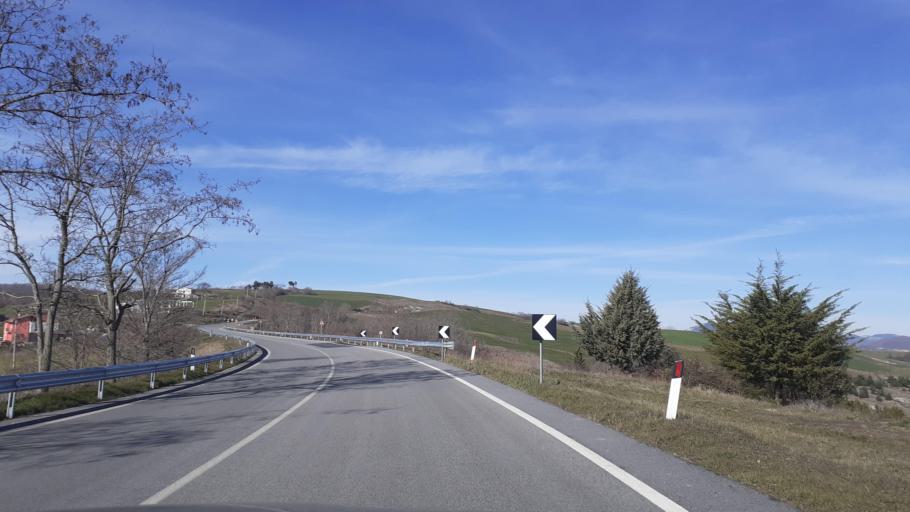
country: IT
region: Molise
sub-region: Provincia di Campobasso
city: Pietracupa
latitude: 41.6851
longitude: 14.5132
